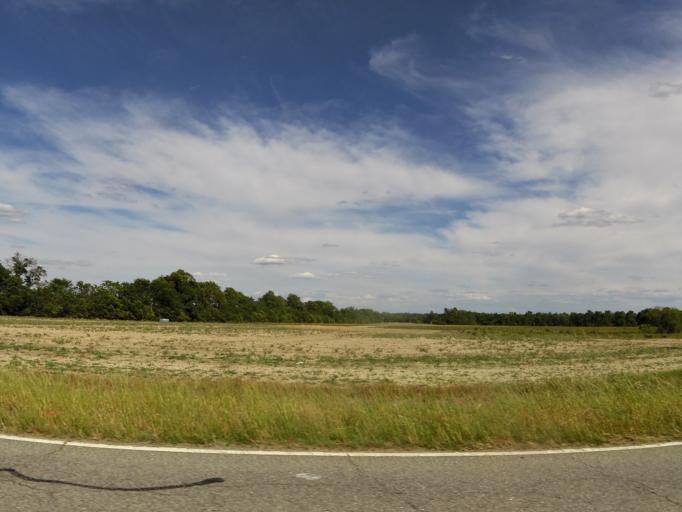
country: US
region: South Carolina
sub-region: Bamberg County
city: Denmark
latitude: 33.1918
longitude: -81.1811
